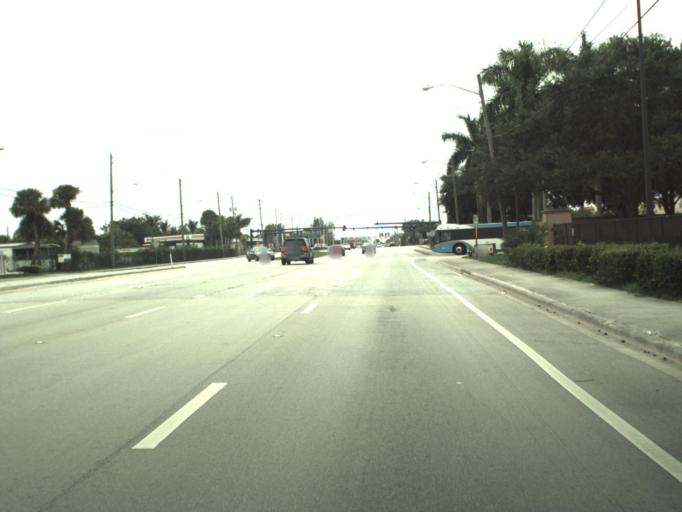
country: US
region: Florida
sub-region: Palm Beach County
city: North Palm Beach
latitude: 26.7861
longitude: -80.1073
